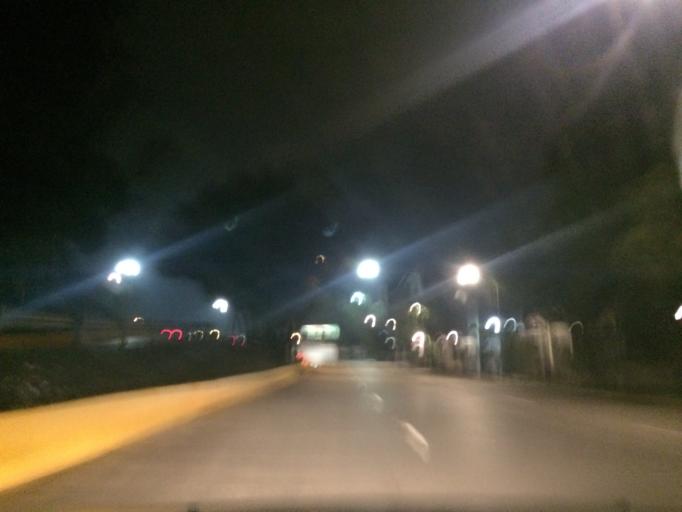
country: MX
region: Mexico City
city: Coyoacan
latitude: 19.3573
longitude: -99.1414
